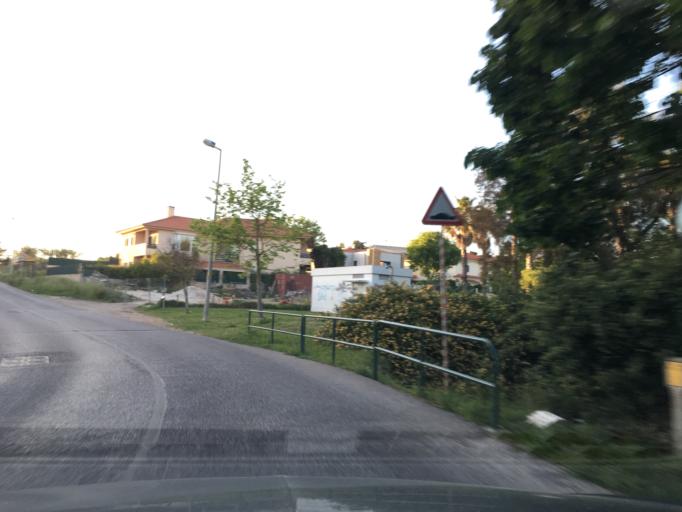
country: PT
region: Lisbon
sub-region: Oeiras
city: Quejas
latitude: 38.7121
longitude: -9.2708
